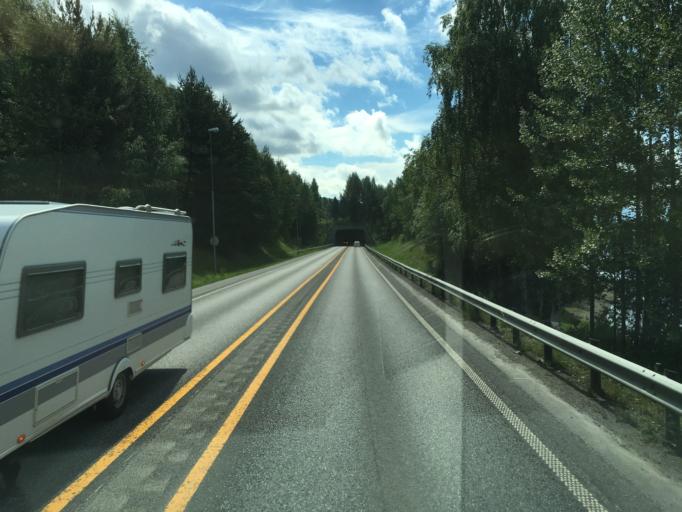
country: NO
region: Oppland
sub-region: Lillehammer
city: Lillehammer
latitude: 61.1244
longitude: 10.4409
